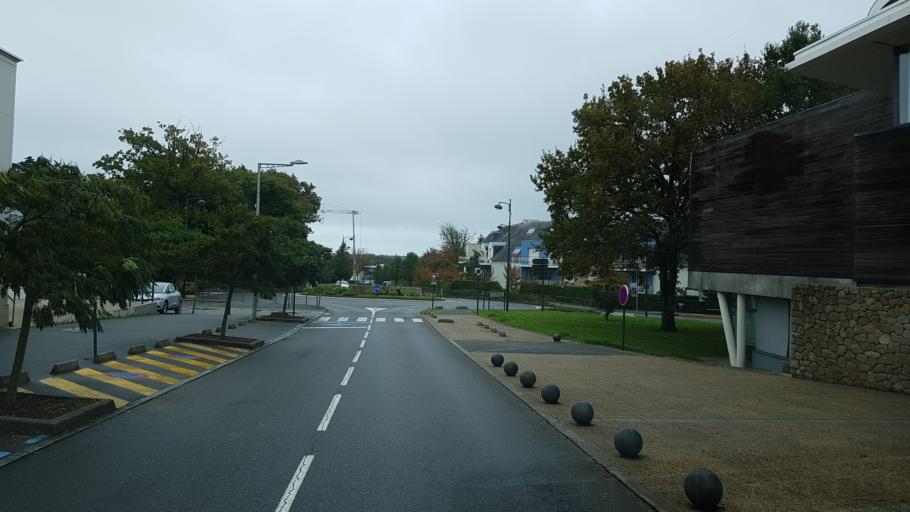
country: FR
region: Brittany
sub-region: Departement du Morbihan
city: Sarzeau
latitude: 47.5246
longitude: -2.7696
